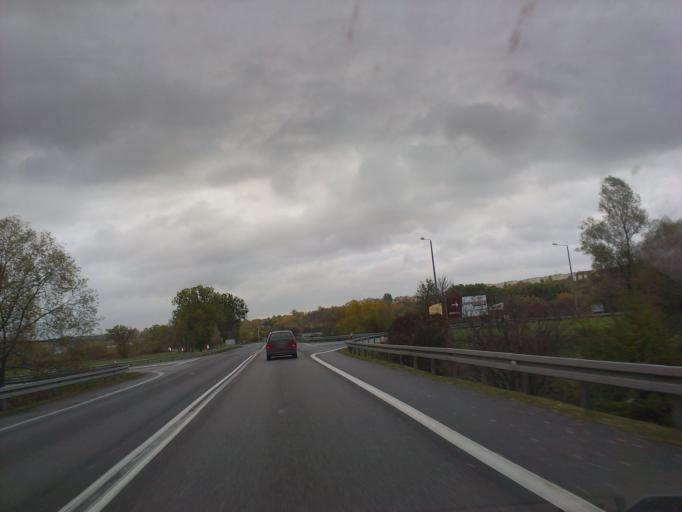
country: PL
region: Kujawsko-Pomorskie
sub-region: Powiat chelminski
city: Chelmno
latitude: 53.3624
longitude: 18.4354
